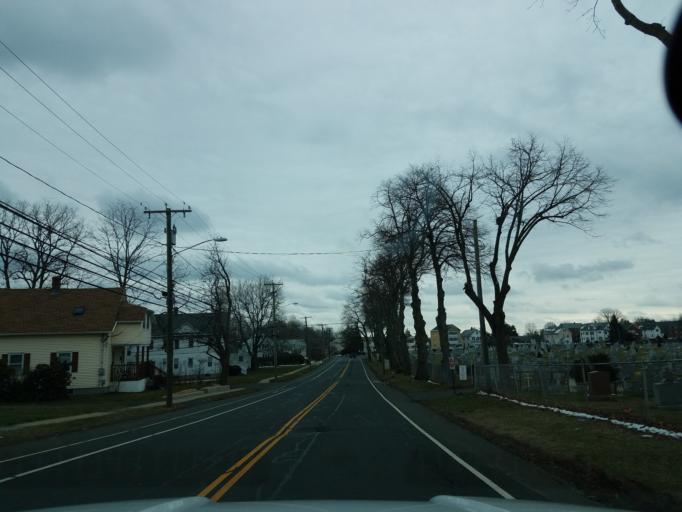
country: US
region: Connecticut
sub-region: Hartford County
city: New Britain
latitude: 41.6842
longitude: -72.7960
